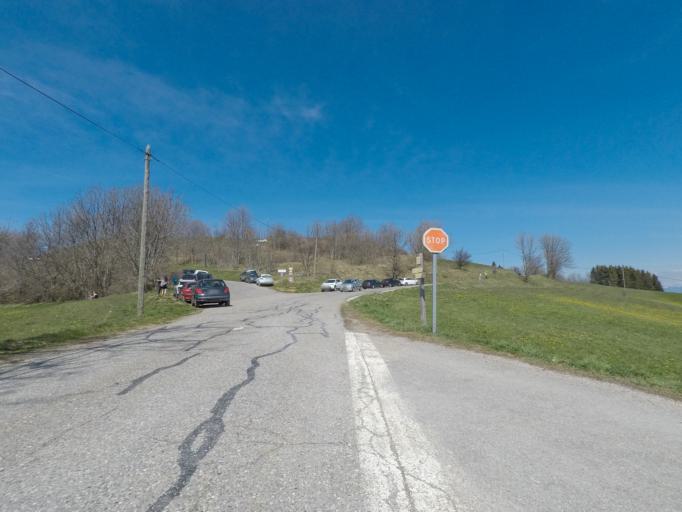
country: FR
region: Rhone-Alpes
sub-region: Departement de la Haute-Savoie
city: Collonges-sous-Saleve
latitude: 46.1253
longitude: 6.1722
